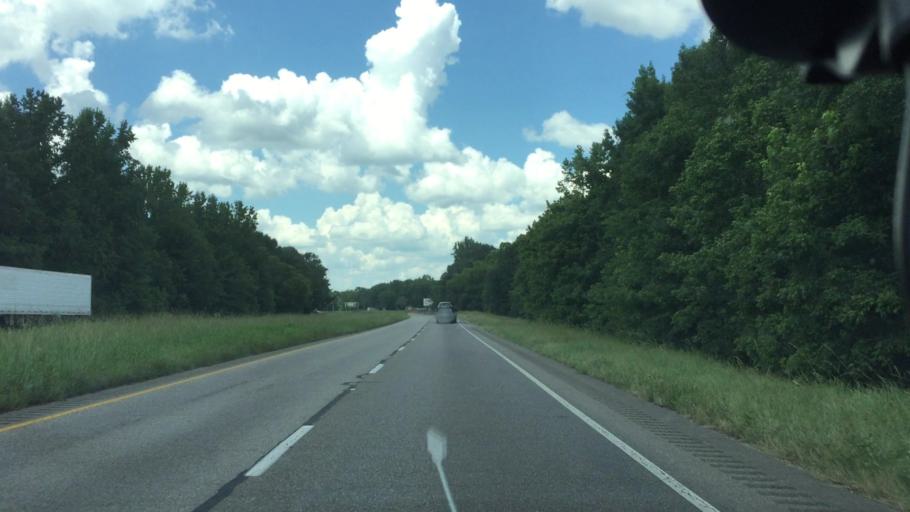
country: US
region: Alabama
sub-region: Montgomery County
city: Pike Road
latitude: 32.1085
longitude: -86.0658
